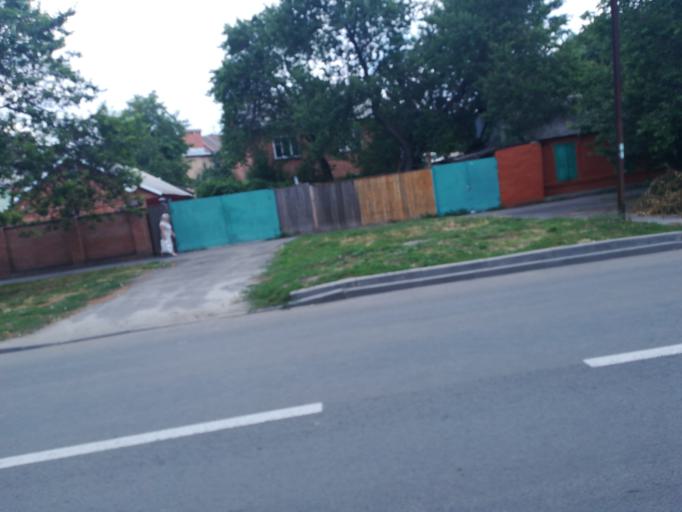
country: RU
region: Rostov
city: Imeni Chkalova
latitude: 47.2532
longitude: 39.7733
